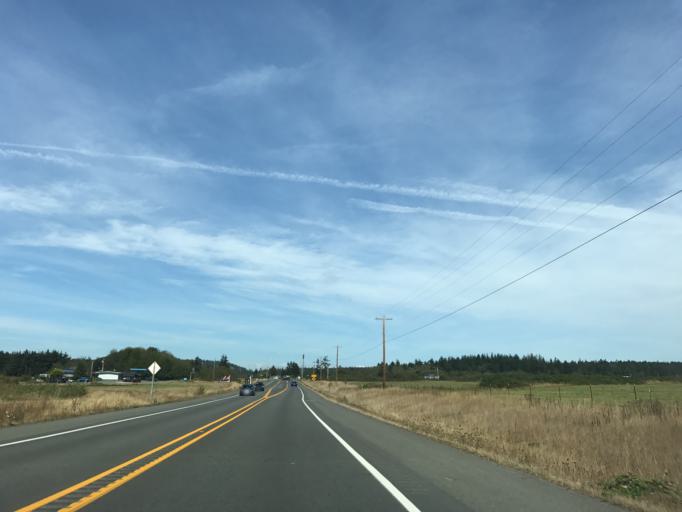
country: US
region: Washington
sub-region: Island County
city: Ault Field
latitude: 48.3735
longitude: -122.6536
